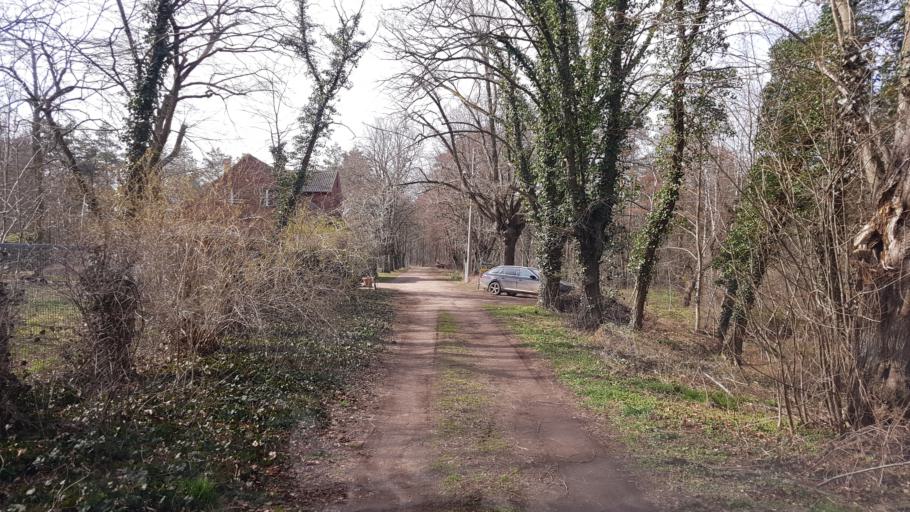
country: DE
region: Brandenburg
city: Doberlug-Kirchhain
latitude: 51.6247
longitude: 13.6166
